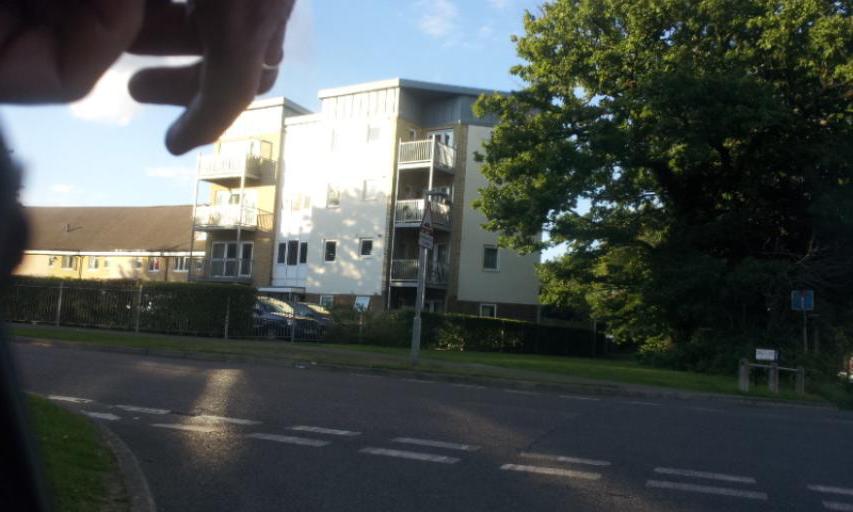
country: GB
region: England
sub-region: Kent
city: Maidstone
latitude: 51.2424
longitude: 0.5569
